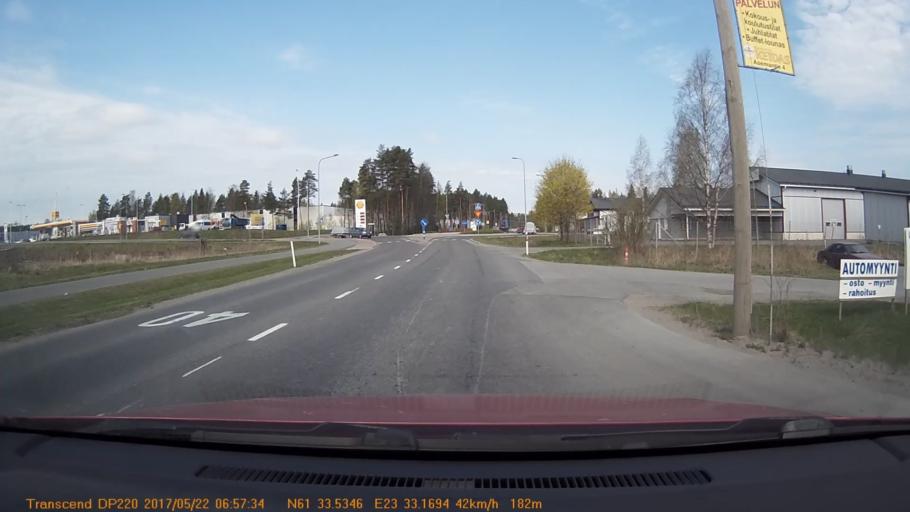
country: FI
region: Pirkanmaa
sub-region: Tampere
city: Yloejaervi
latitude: 61.5589
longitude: 23.5527
